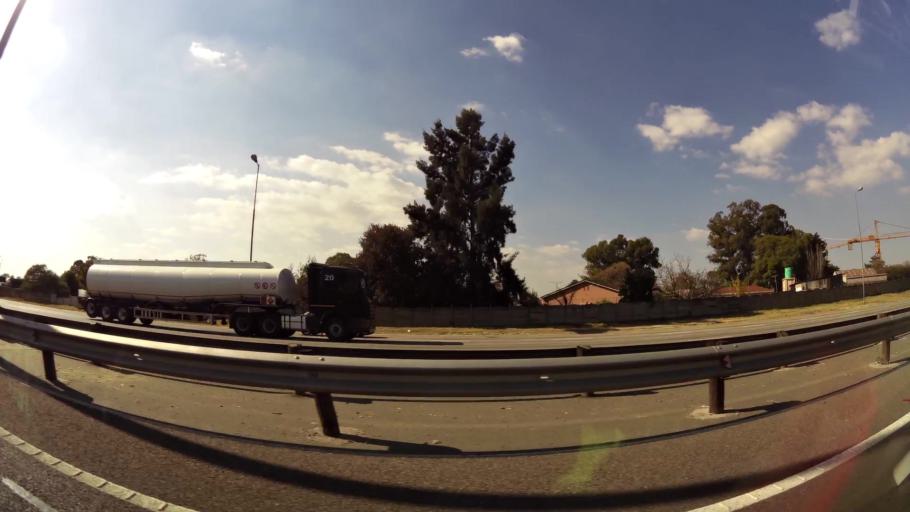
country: ZA
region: Gauteng
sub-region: Ekurhuleni Metropolitan Municipality
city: Tembisa
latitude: -26.0874
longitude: 28.2698
